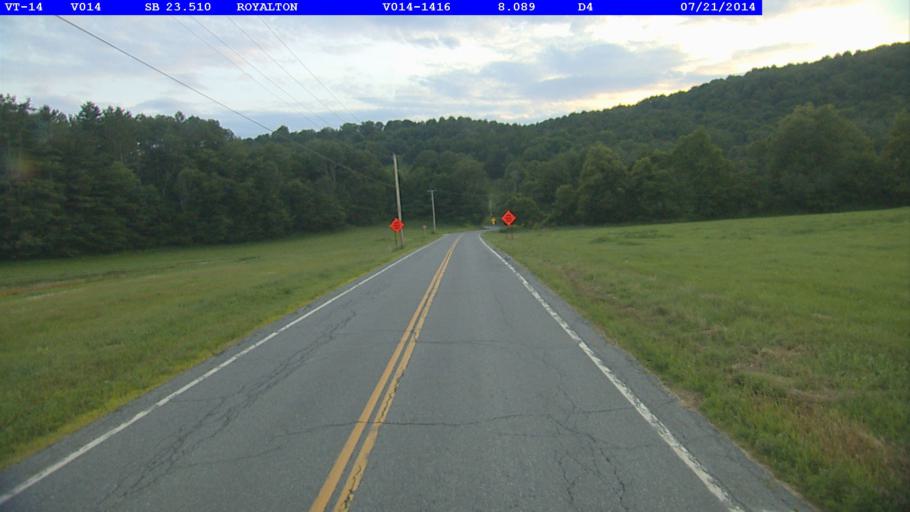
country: US
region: Vermont
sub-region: Orange County
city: Randolph
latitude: 43.8497
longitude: -72.5846
